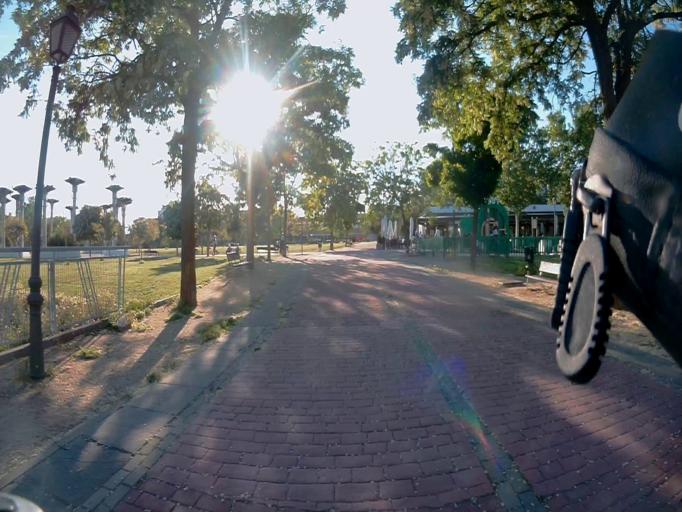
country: ES
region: Madrid
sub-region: Provincia de Madrid
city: Alcorcon
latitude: 40.3428
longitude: -3.8367
